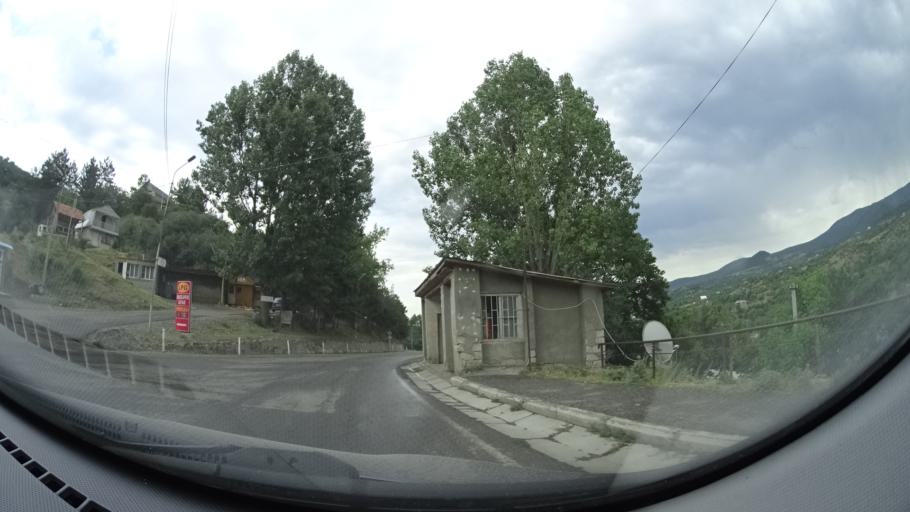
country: GE
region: Samtskhe-Javakheti
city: Adigeni
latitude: 41.6750
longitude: 42.7069
